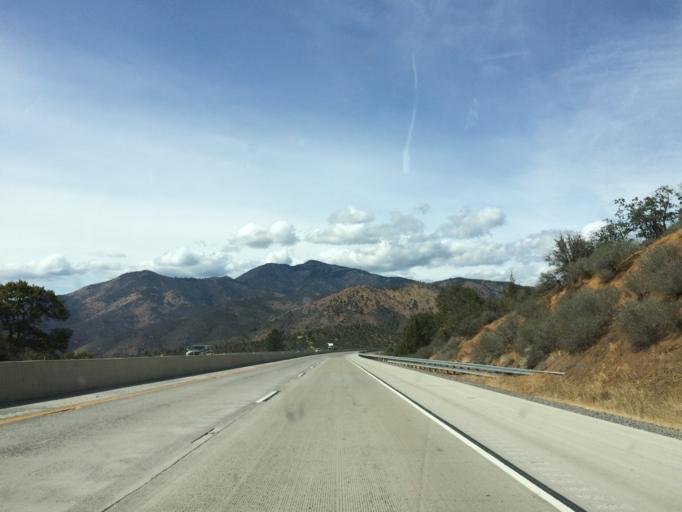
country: US
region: California
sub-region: Siskiyou County
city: Montague
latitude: 41.8137
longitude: -122.5730
